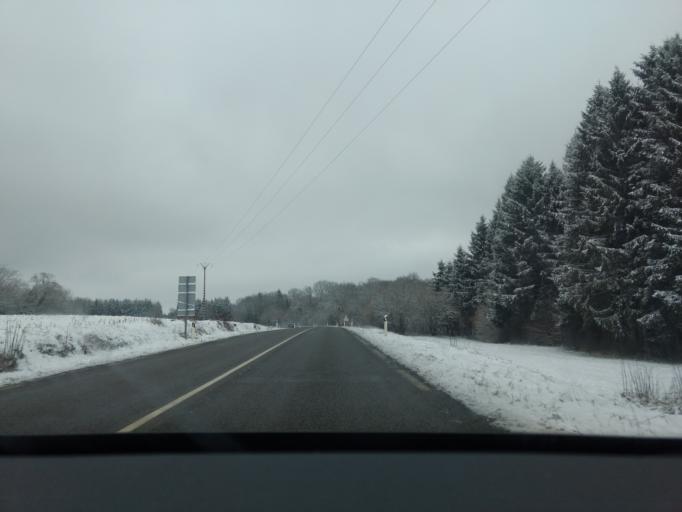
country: FR
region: Franche-Comte
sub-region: Departement du Jura
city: Champagnole
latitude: 46.7852
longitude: 5.8550
